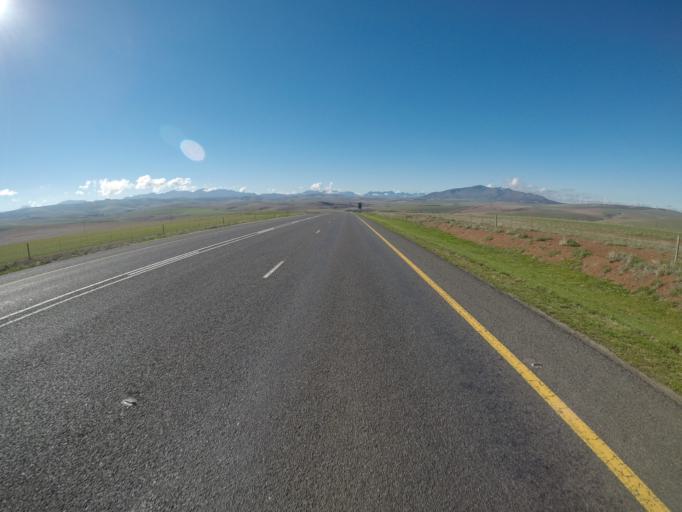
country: ZA
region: Western Cape
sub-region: Overberg District Municipality
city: Caledon
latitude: -34.2176
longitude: 19.3166
